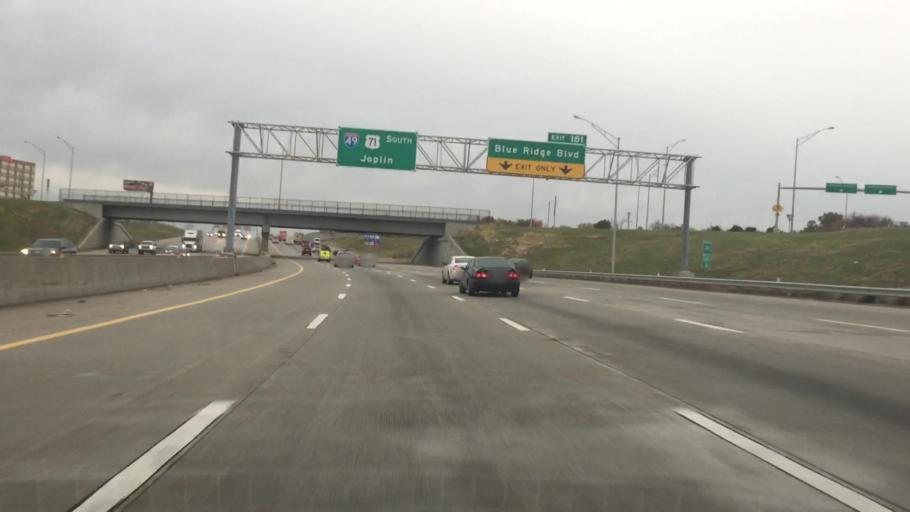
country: US
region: Missouri
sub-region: Jackson County
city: Grandview
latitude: 38.9178
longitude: -94.5276
